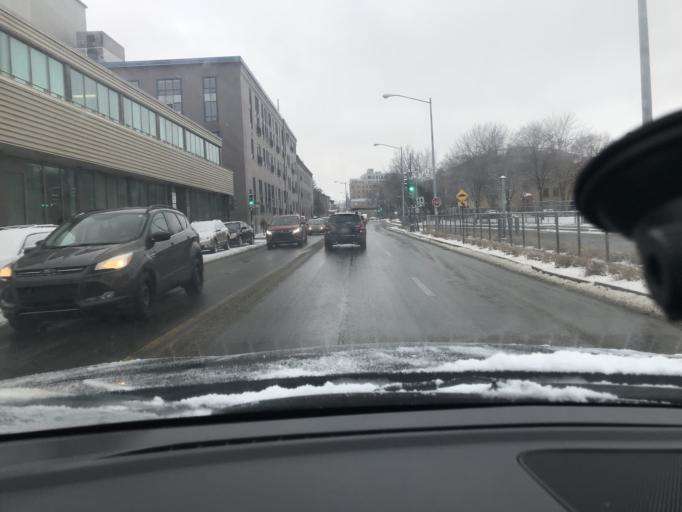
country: CA
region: Quebec
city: Quebec
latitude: 46.8171
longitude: -71.2245
